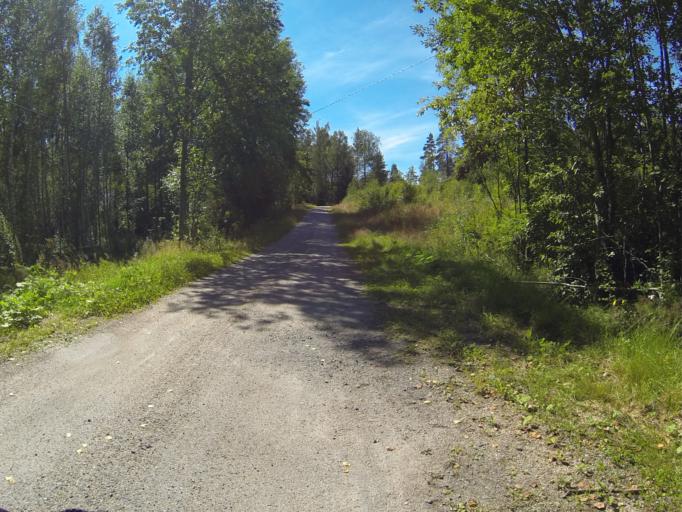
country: FI
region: Varsinais-Suomi
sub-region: Salo
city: Salo
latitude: 60.2994
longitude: 23.1041
